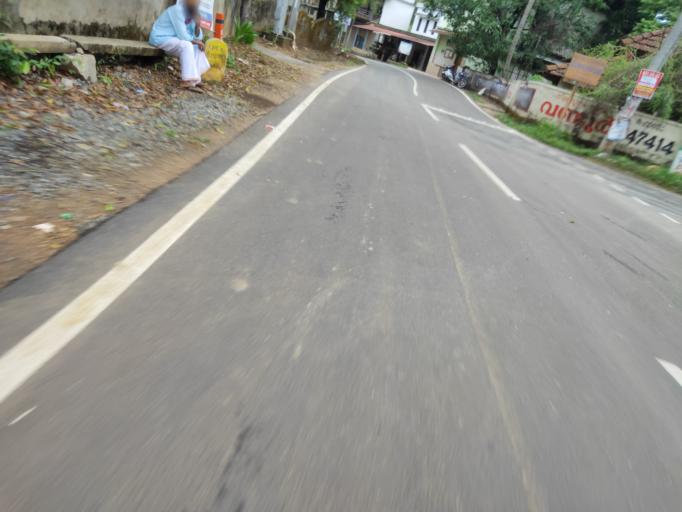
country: IN
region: Kerala
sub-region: Malappuram
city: Manjeri
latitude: 11.1867
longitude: 76.2147
